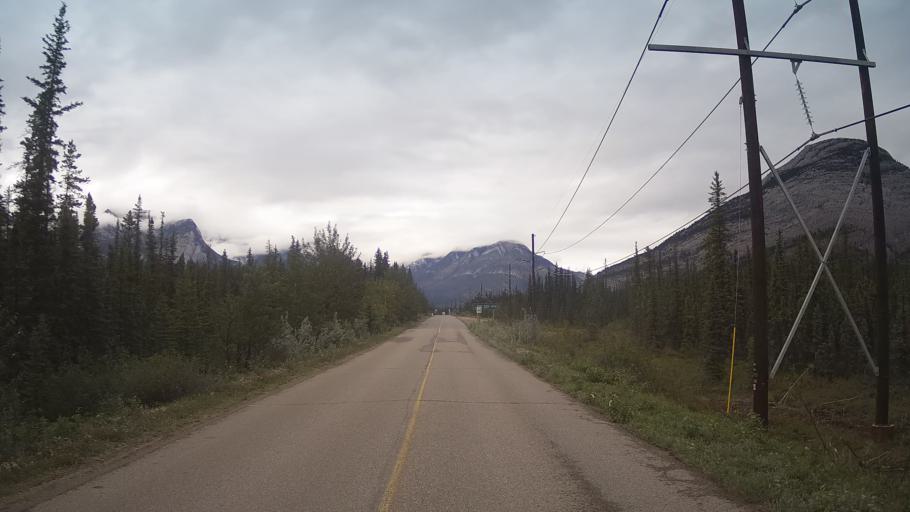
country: CA
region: Alberta
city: Jasper Park Lodge
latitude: 53.0073
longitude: -118.0860
